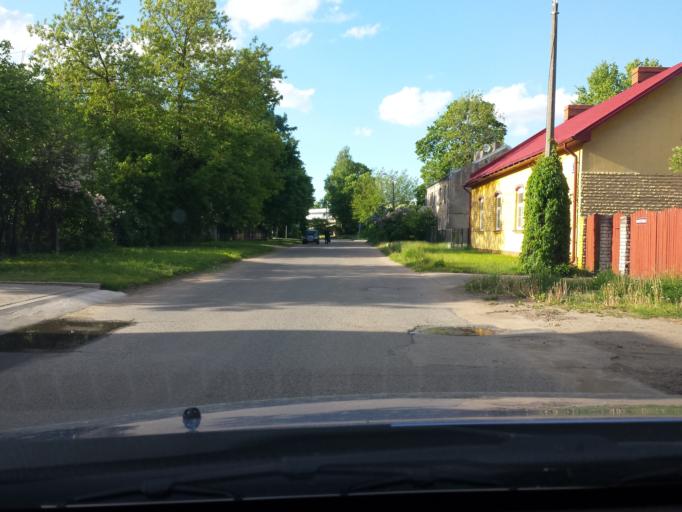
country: LV
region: Riga
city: Jaunciems
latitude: 56.9825
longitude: 24.1601
